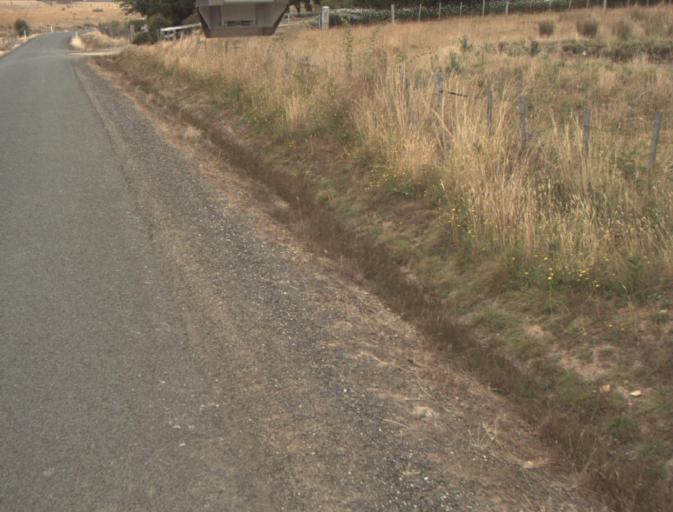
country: AU
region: Tasmania
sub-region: Northern Midlands
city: Evandale
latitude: -41.5219
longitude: 147.3905
